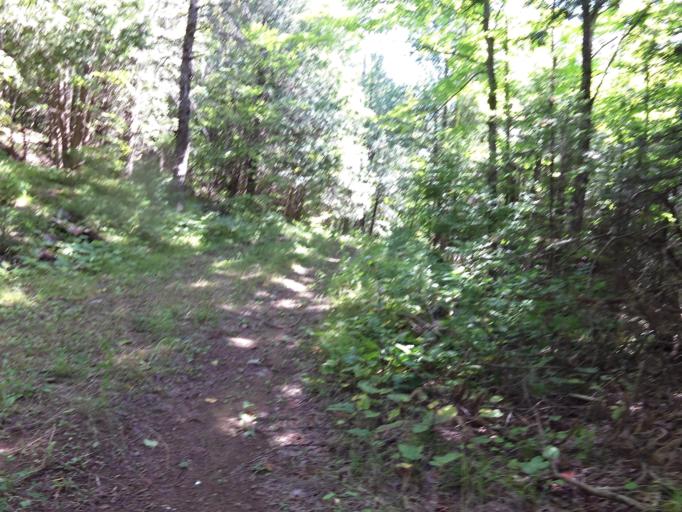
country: CA
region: Ontario
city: Renfrew
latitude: 45.0272
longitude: -76.7001
